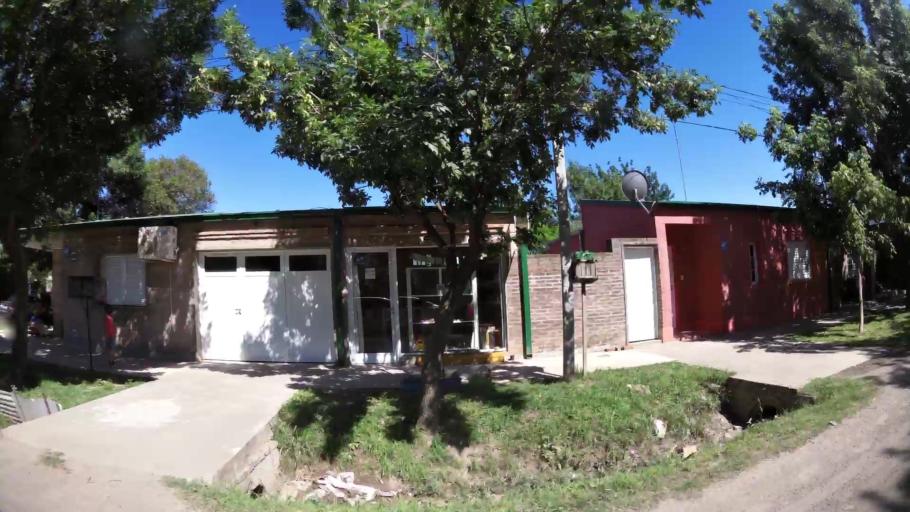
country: AR
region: Santa Fe
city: Esperanza
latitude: -31.4541
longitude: -60.9427
